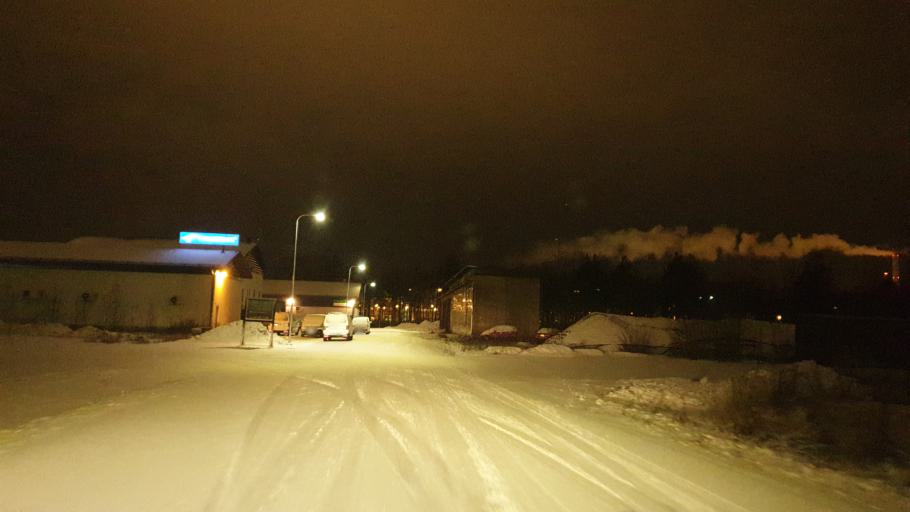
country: FI
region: Northern Ostrobothnia
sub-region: Oulu
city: Oulu
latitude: 64.9953
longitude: 25.4411
